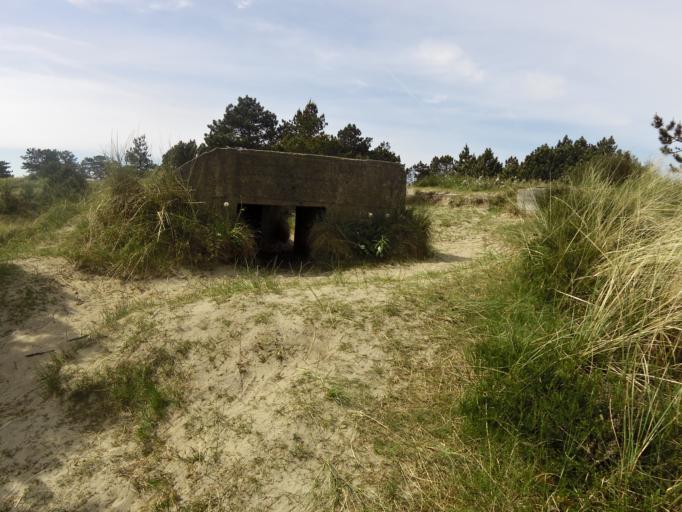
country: DE
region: Schleswig-Holstein
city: List
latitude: 55.1514
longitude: 8.5317
